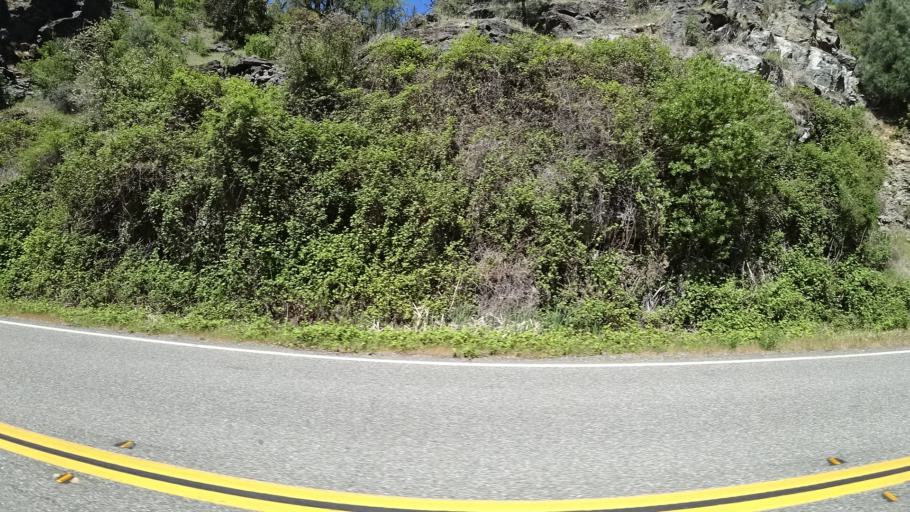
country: US
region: California
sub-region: Trinity County
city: Hayfork
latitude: 40.7520
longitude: -123.1630
